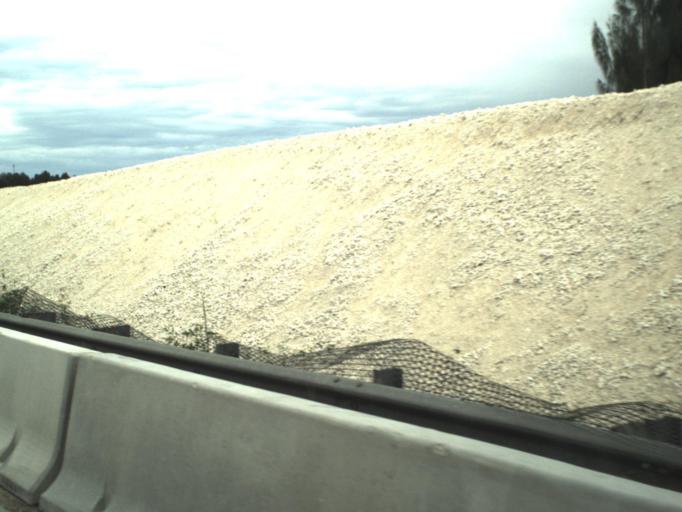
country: US
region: Florida
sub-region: Miami-Dade County
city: Kendall West
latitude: 25.7505
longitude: -80.4810
